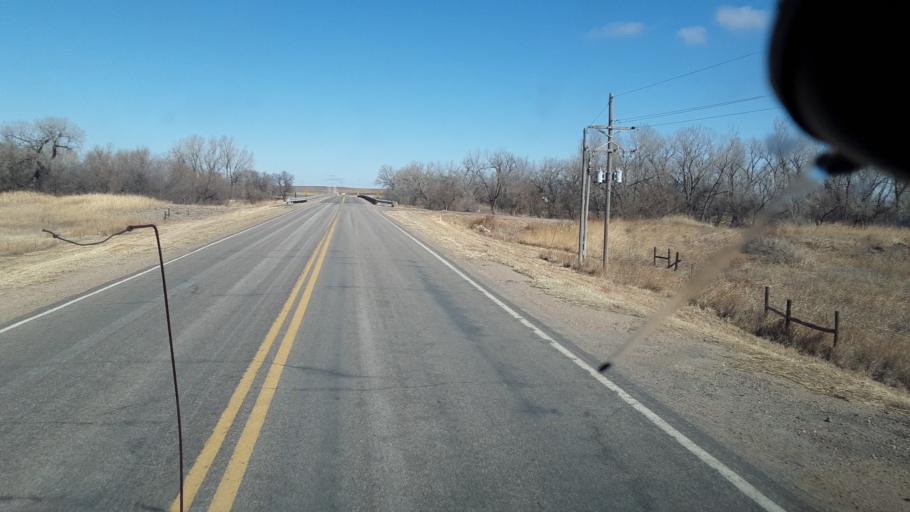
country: US
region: Kansas
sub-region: Barton County
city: Ellinwood
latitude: 38.3545
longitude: -98.6641
